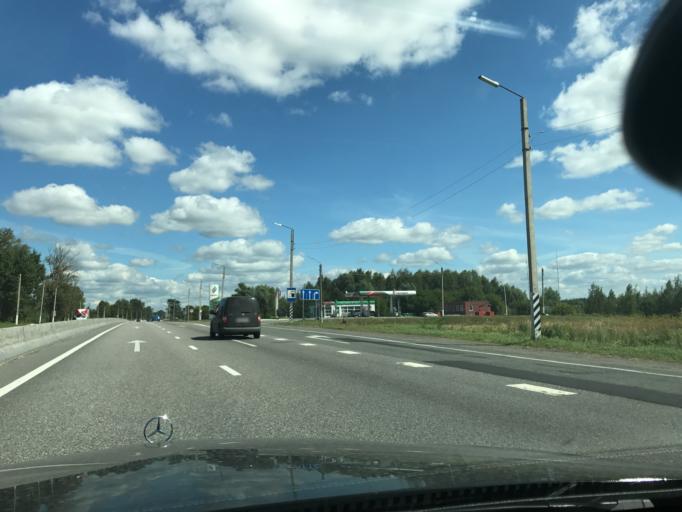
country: RU
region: Nizjnij Novgorod
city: Mulino
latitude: 56.2737
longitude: 42.9635
